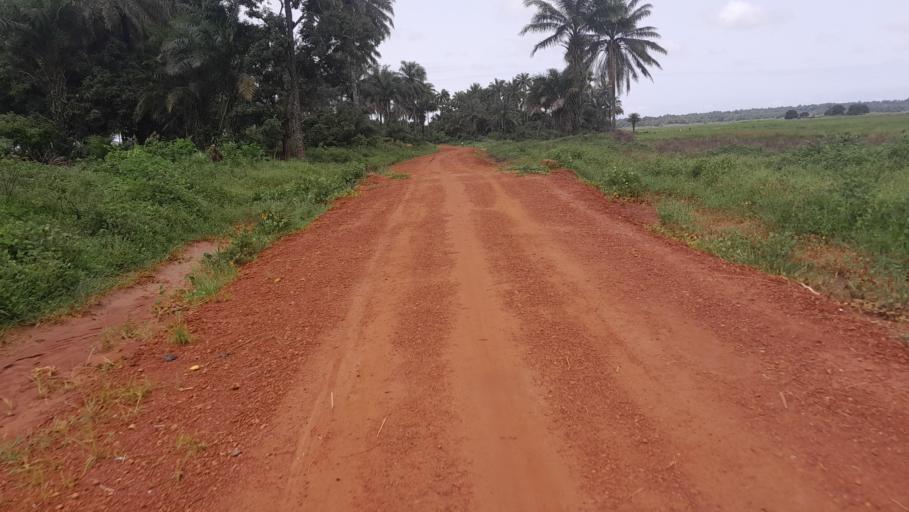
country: GN
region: Boke
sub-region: Boffa
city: Boffa
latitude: 9.9971
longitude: -13.8880
